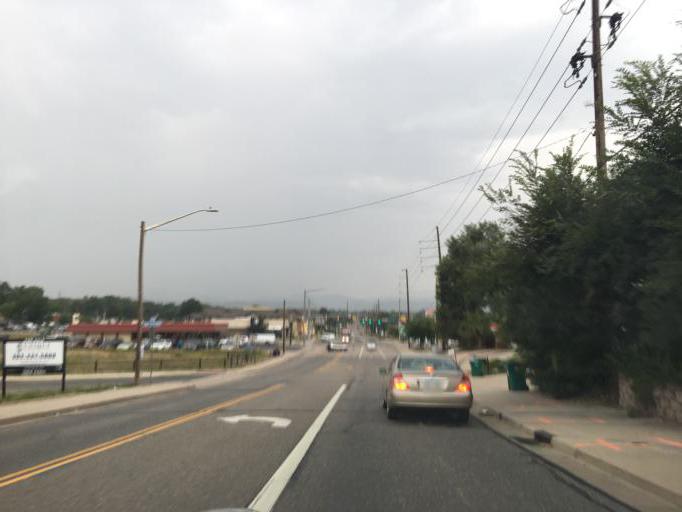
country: US
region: Colorado
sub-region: Jefferson County
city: Wheat Ridge
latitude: 39.7694
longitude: -105.1078
